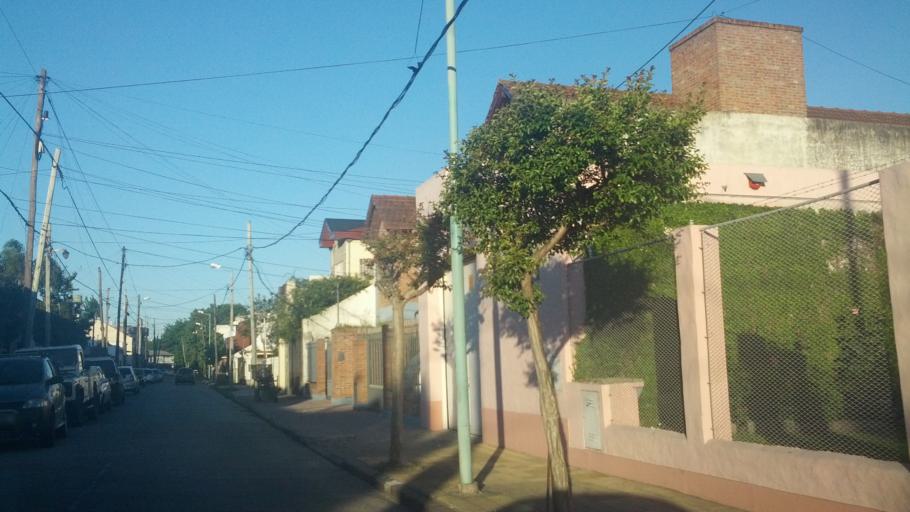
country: AR
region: Buenos Aires
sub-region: Partido de Lomas de Zamora
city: Lomas de Zamora
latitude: -34.7809
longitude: -58.4080
